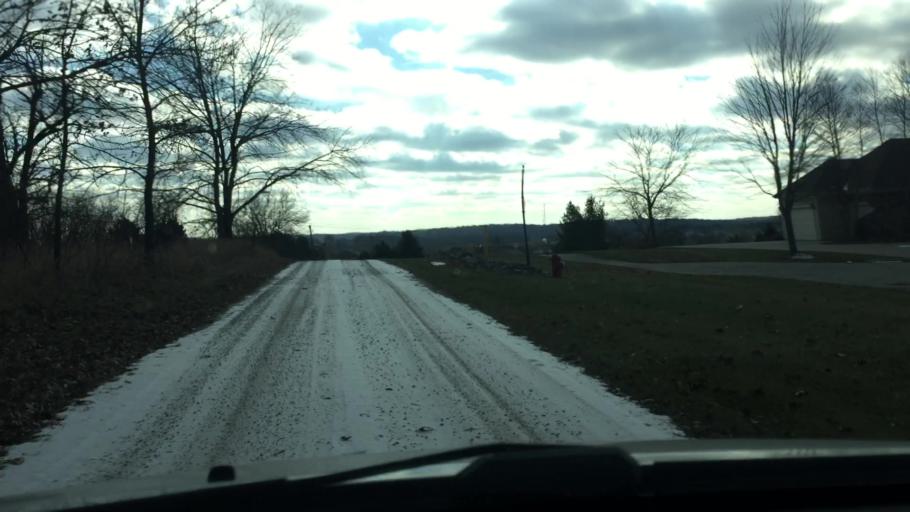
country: US
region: Wisconsin
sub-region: Waukesha County
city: Merton
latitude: 43.1210
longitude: -88.3180
